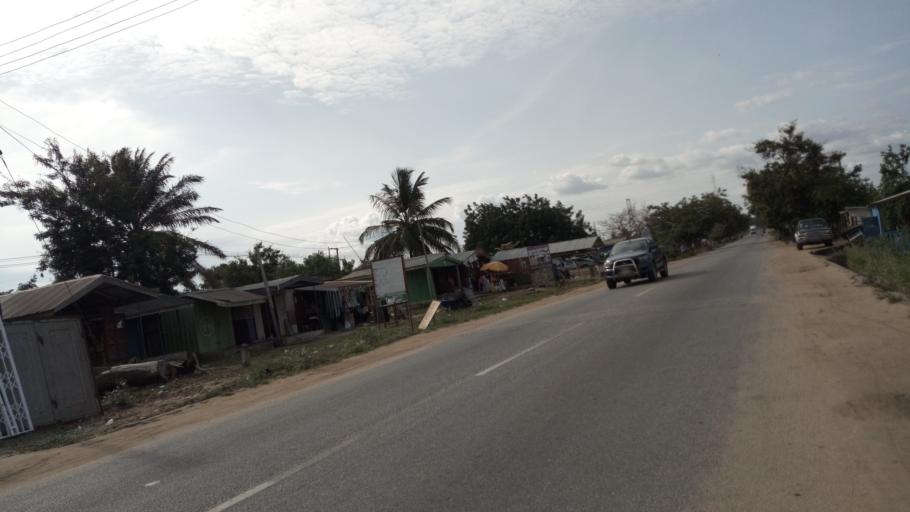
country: GH
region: Central
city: Winneba
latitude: 5.3854
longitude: -0.6436
